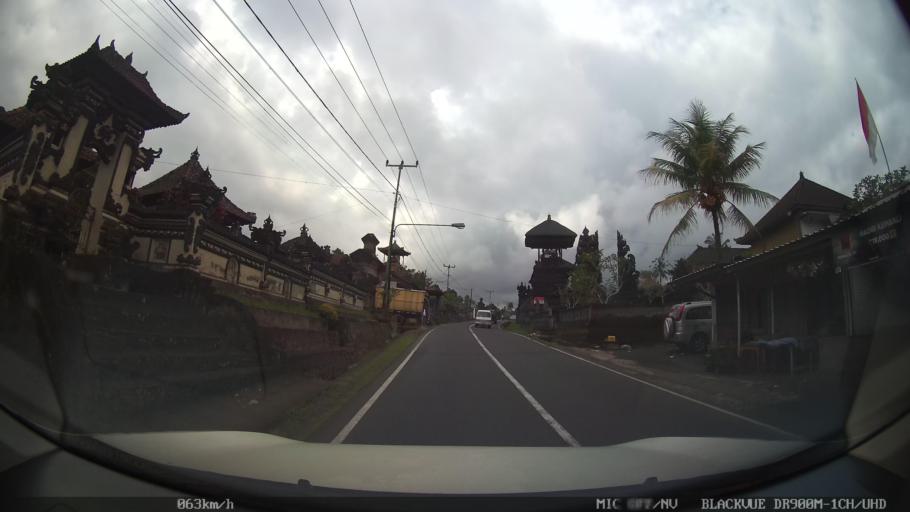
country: ID
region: Bali
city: Banjar Kubu
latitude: -8.3973
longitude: 115.4201
